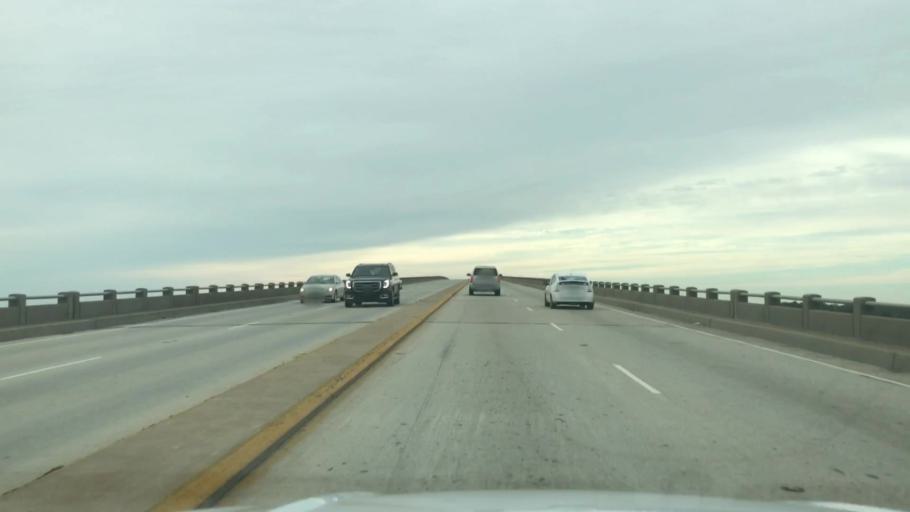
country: US
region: South Carolina
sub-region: Georgetown County
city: Georgetown
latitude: 33.3653
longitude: -79.2492
